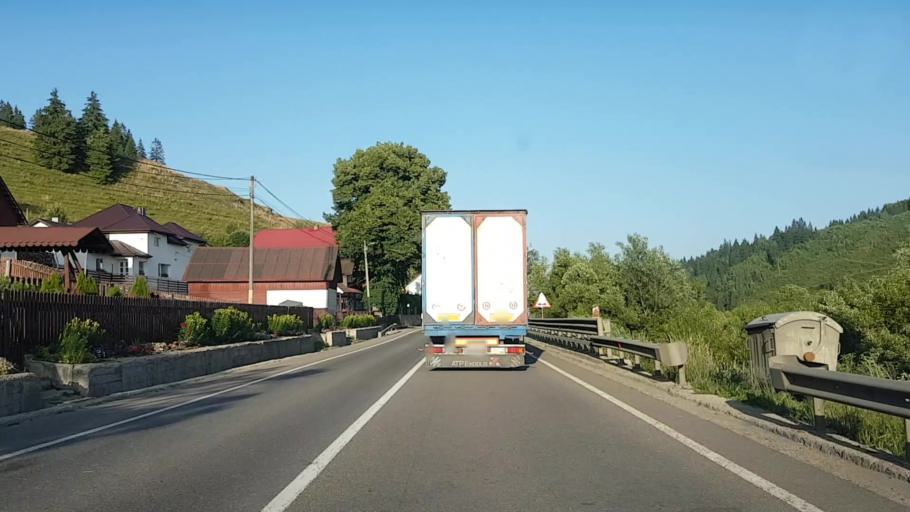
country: RO
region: Suceava
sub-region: Comuna Dorna Candrenilor
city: Dorna Candrenilor
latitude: 47.3568
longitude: 25.2779
